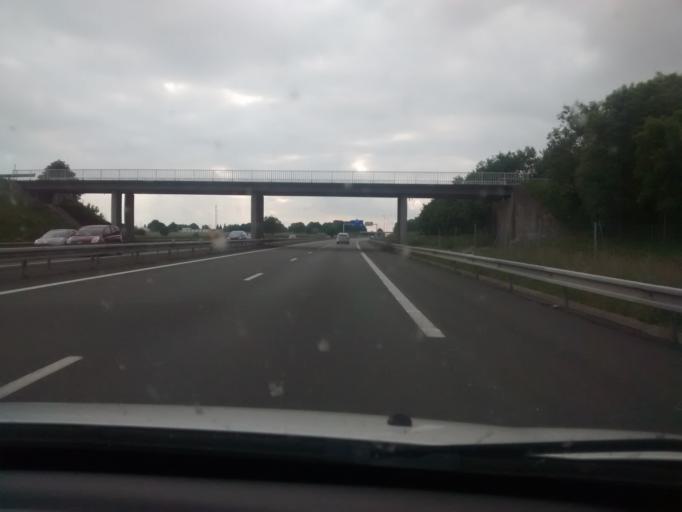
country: FR
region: Pays de la Loire
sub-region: Departement de la Sarthe
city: Brulon
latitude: 48.0039
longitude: -0.2050
